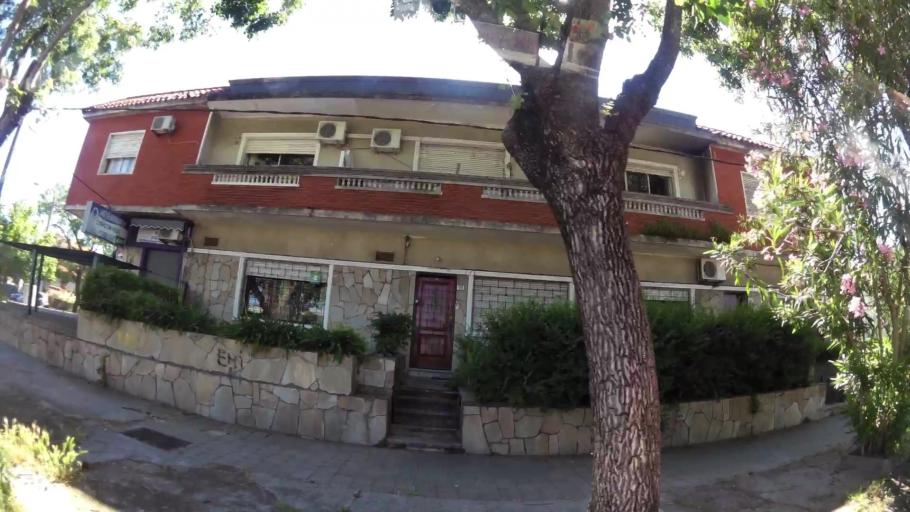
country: UY
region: Montevideo
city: Montevideo
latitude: -34.8890
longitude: -56.1428
